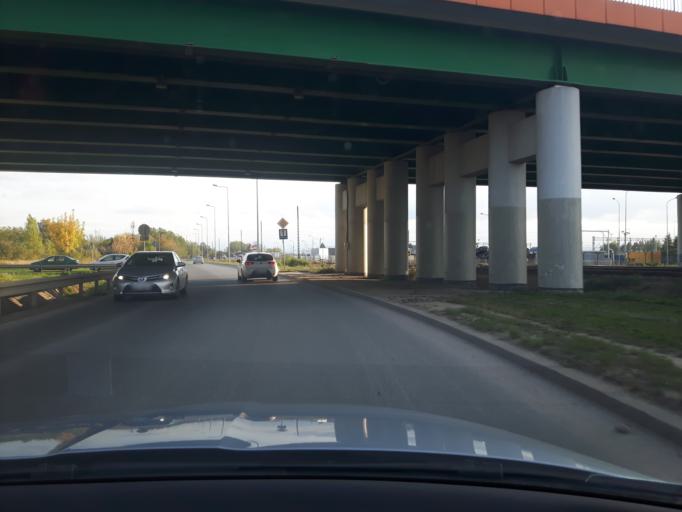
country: PL
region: Masovian Voivodeship
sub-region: Warszawa
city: Wlochy
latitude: 52.1568
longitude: 20.9904
